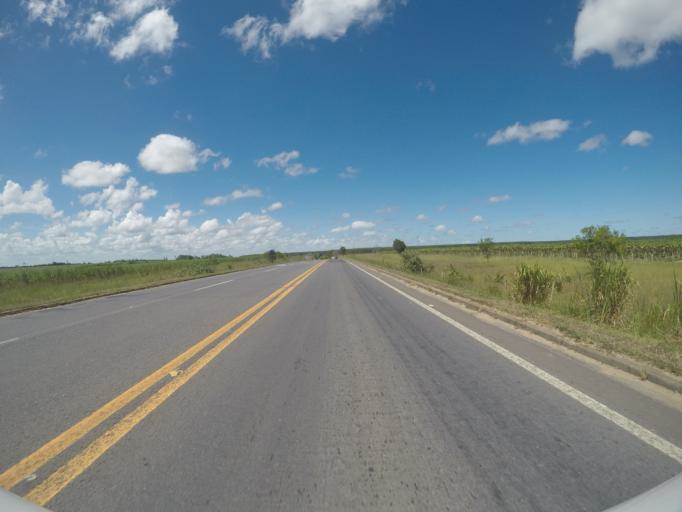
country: BR
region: Espirito Santo
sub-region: Conceicao Da Barra
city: Conceicao da Barra
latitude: -18.2641
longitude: -39.9566
